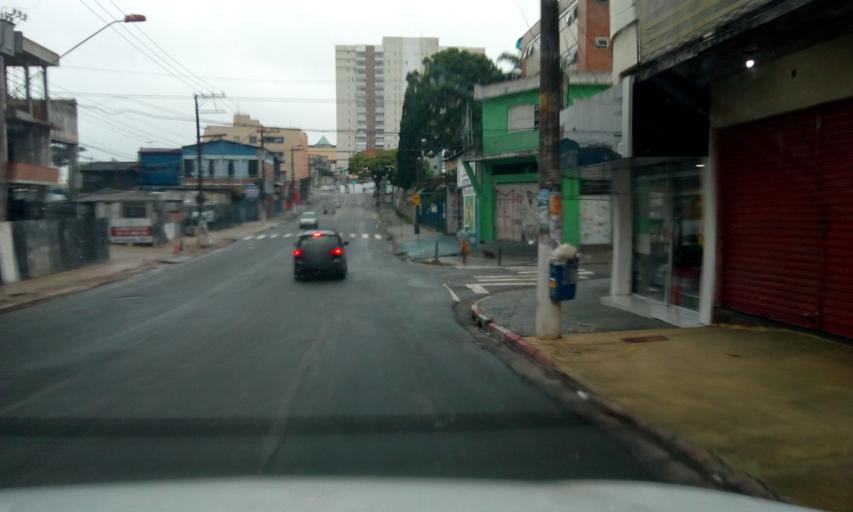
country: BR
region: Sao Paulo
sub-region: Diadema
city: Diadema
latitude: -23.6943
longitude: -46.6286
